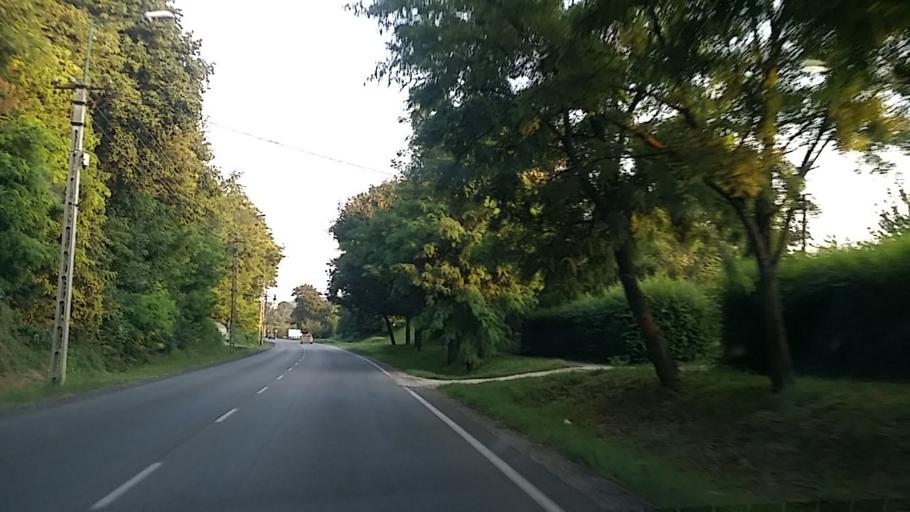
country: HU
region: Fejer
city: dunaujvaros
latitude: 46.9880
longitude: 18.9312
